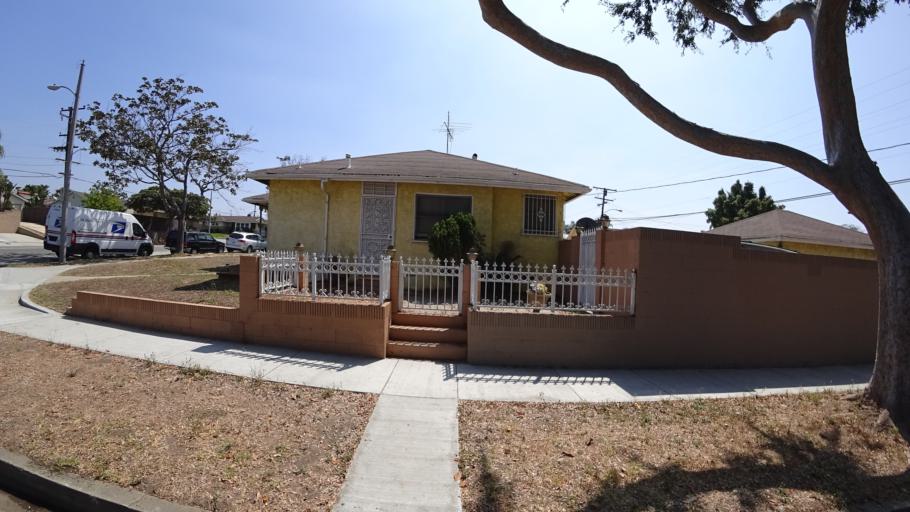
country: US
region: California
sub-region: Los Angeles County
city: Westmont
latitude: 33.9380
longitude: -118.3228
